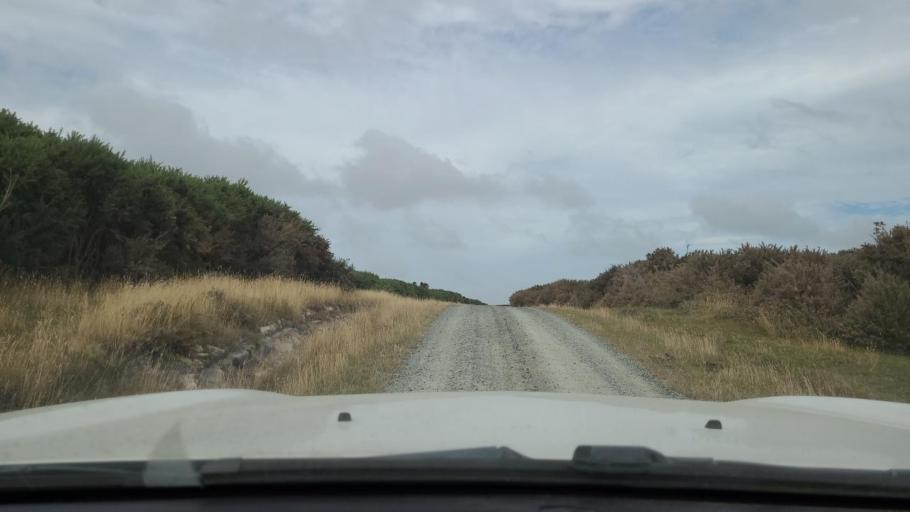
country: NZ
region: Chatham Islands
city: Waitangi
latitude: -43.9191
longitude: -176.4915
